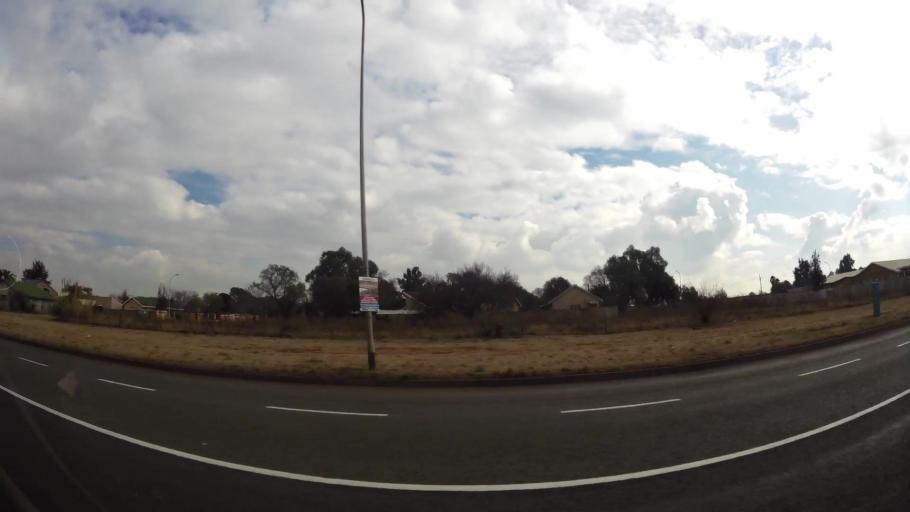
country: ZA
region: Gauteng
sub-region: Sedibeng District Municipality
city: Meyerton
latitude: -26.5931
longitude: 27.9961
